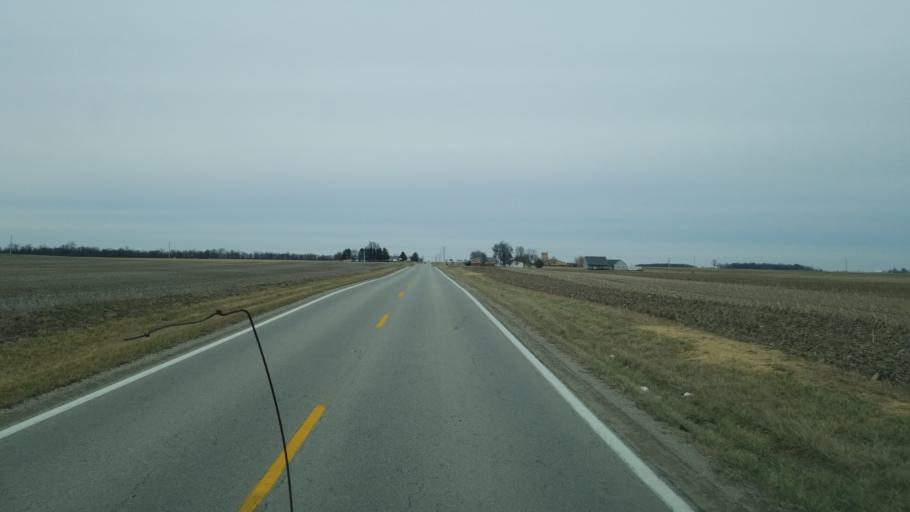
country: US
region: Ohio
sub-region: Ross County
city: Frankfort
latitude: 39.4523
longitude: -83.2128
